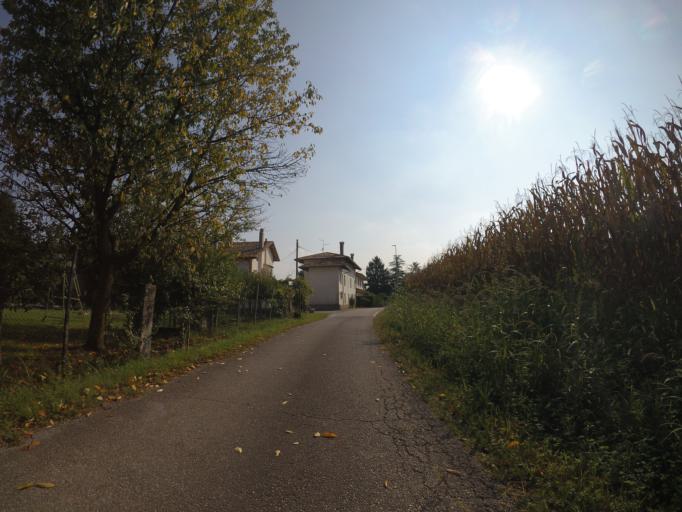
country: IT
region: Friuli Venezia Giulia
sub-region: Provincia di Udine
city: Camino al Tagliamento
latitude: 45.8981
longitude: 12.9549
